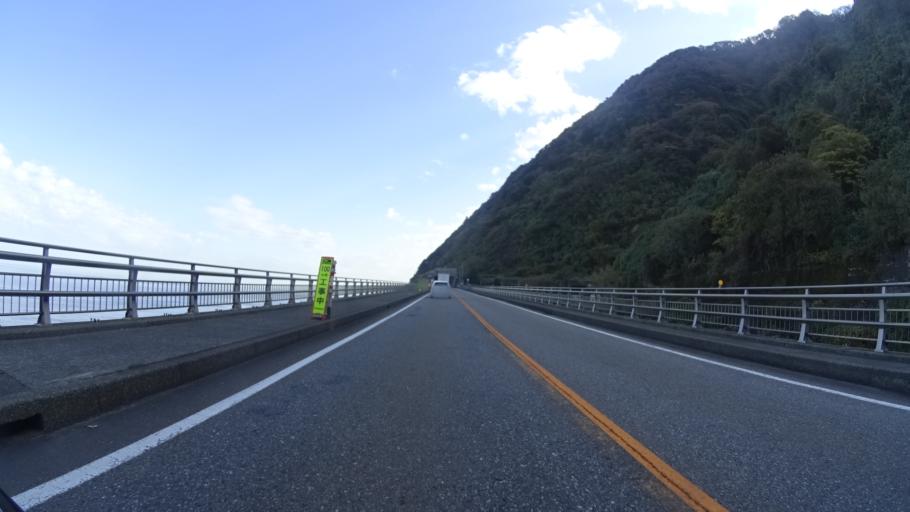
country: JP
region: Niigata
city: Itoigawa
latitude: 37.0158
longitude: 137.7630
